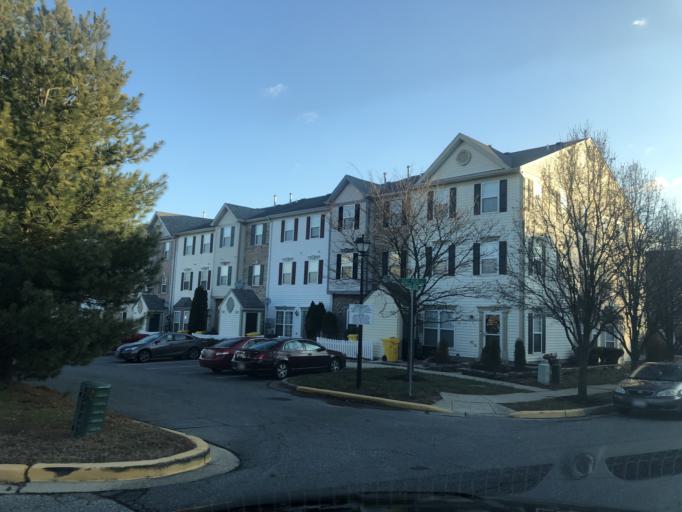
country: US
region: Maryland
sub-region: Anne Arundel County
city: Odenton
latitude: 39.1003
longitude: -76.7135
